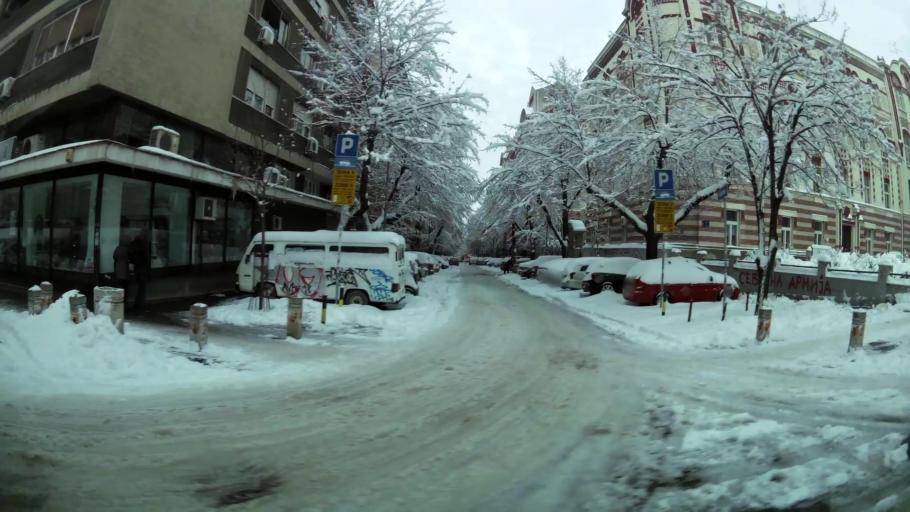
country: RS
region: Central Serbia
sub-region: Belgrade
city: Stari Grad
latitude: 44.8119
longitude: 20.4670
